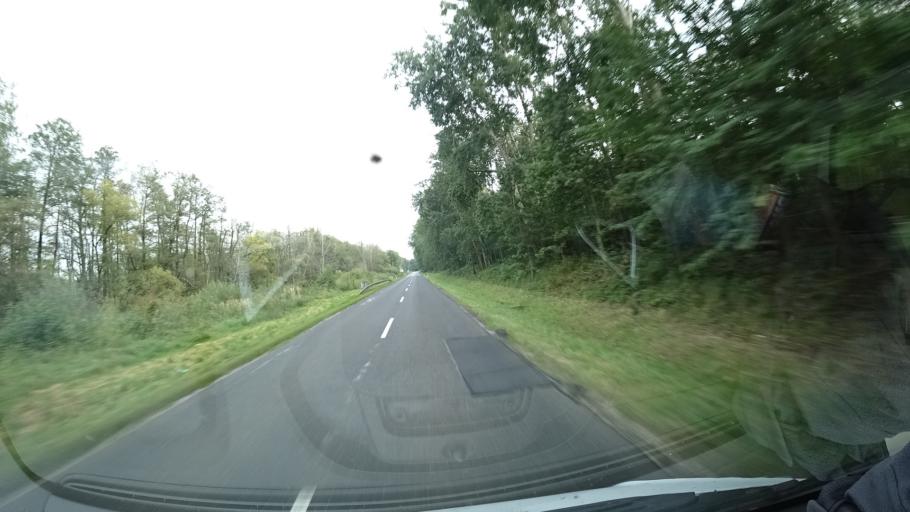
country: PL
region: Silesian Voivodeship
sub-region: Powiat gliwicki
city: Pyskowice
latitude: 50.3910
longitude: 18.5720
